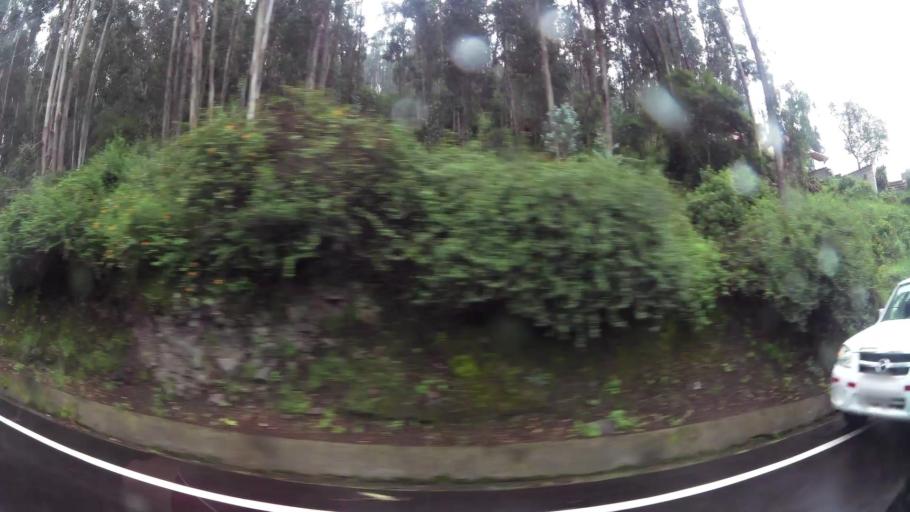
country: EC
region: Pichincha
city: Sangolqui
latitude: -0.2797
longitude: -78.4473
